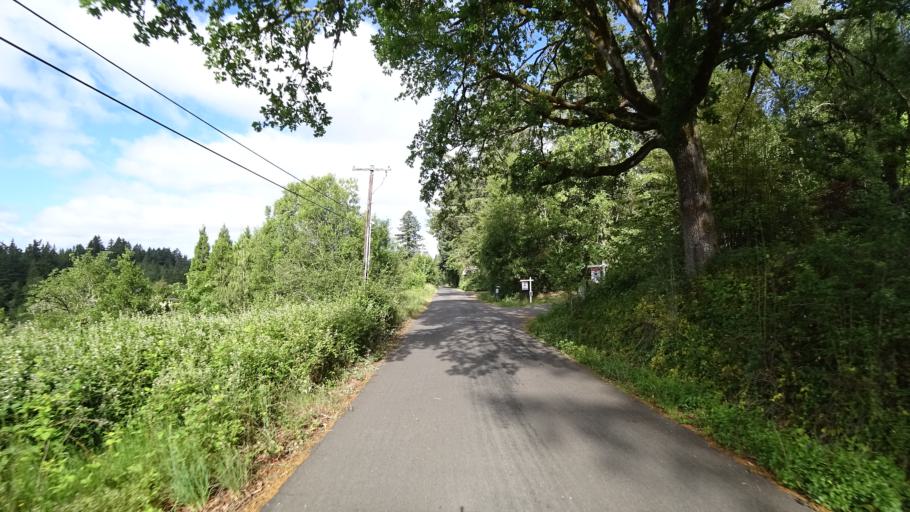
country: US
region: Oregon
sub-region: Washington County
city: Oak Hills
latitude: 45.5811
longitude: -122.8243
